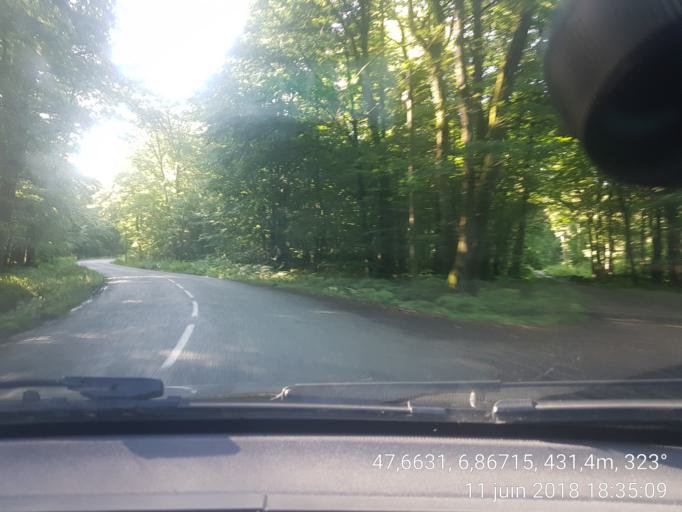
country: FR
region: Franche-Comte
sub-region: Territoire de Belfort
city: Offemont
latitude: 47.6631
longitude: 6.8672
